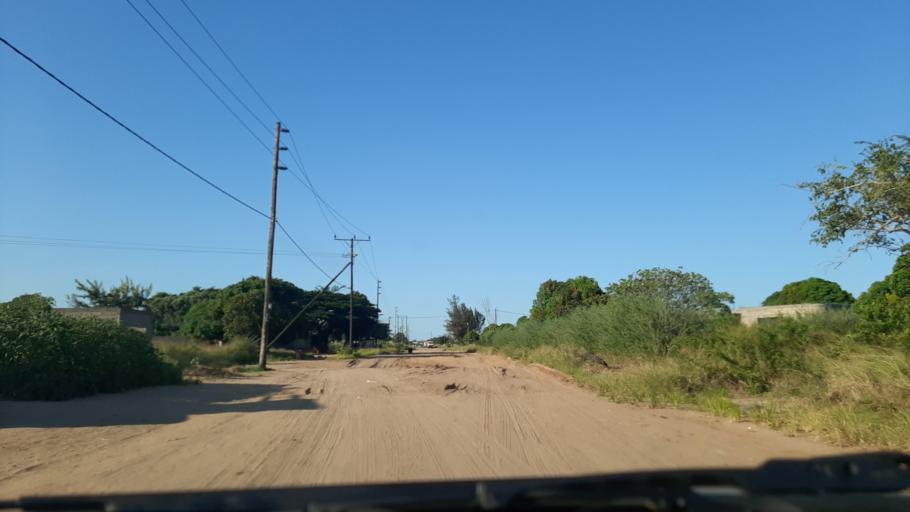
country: MZ
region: Maputo City
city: Maputo
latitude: -25.7622
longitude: 32.5479
